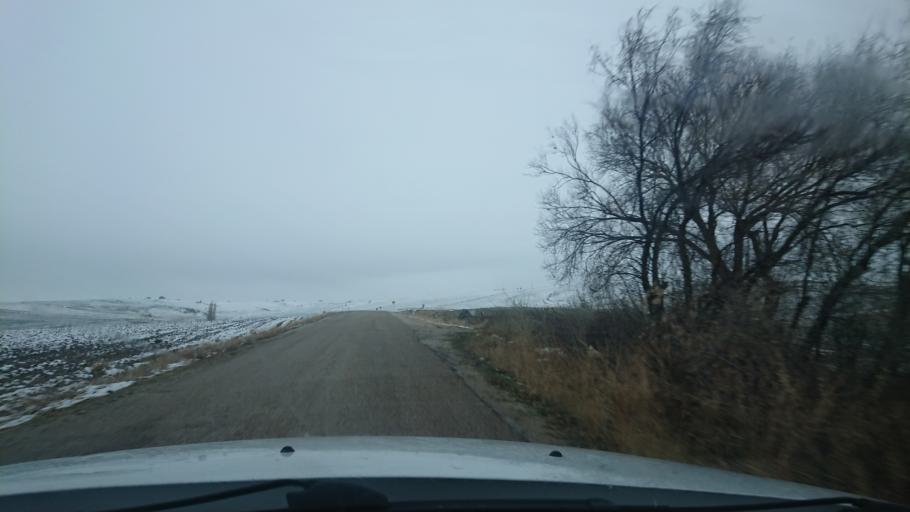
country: TR
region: Aksaray
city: Agacoren
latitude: 38.8494
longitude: 33.9499
